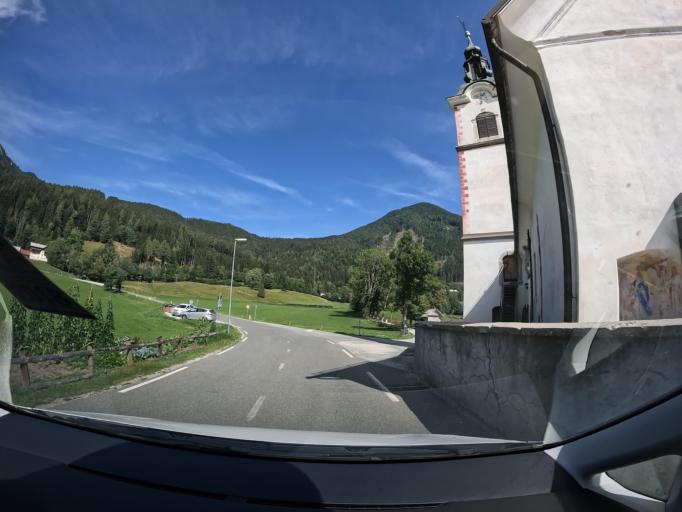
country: AT
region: Carinthia
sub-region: Politischer Bezirk Feldkirchen
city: Glanegg
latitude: 46.7401
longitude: 14.1581
